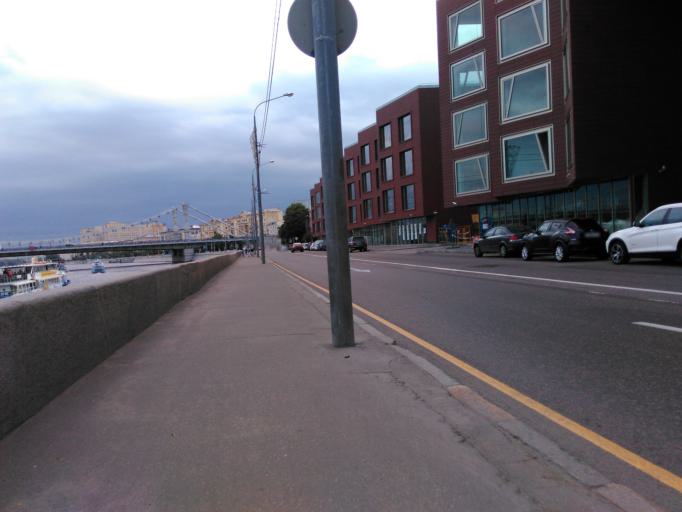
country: RU
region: Moscow
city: Moscow
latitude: 55.7368
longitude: 37.6020
